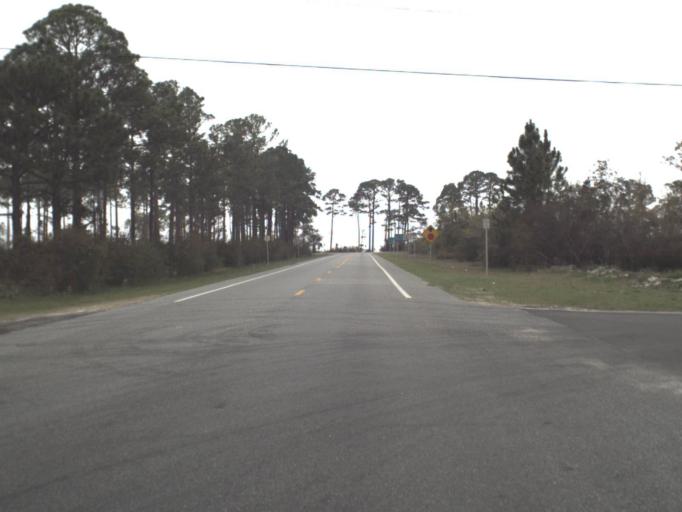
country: US
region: Florida
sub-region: Franklin County
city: Eastpoint
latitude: 29.7601
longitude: -84.8331
